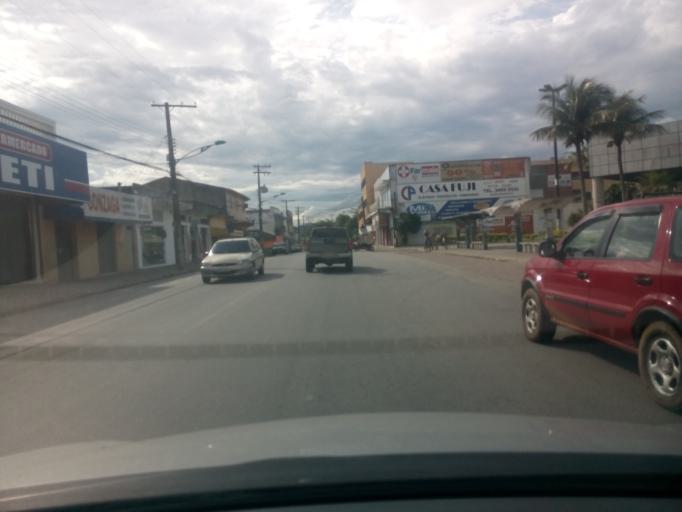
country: BR
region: Sao Paulo
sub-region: Peruibe
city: Peruibe
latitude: -24.3198
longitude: -47.0056
